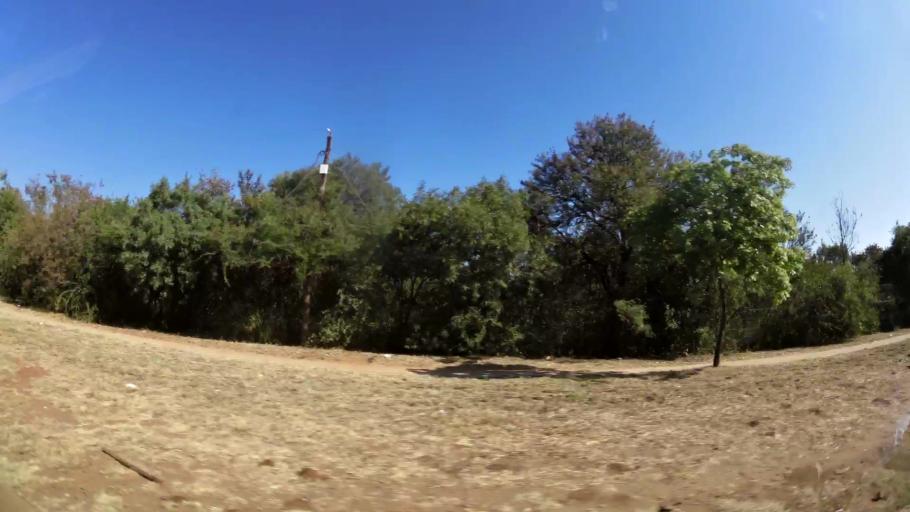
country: ZA
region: Gauteng
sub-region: City of Tshwane Metropolitan Municipality
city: Pretoria
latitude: -25.6700
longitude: 28.2434
